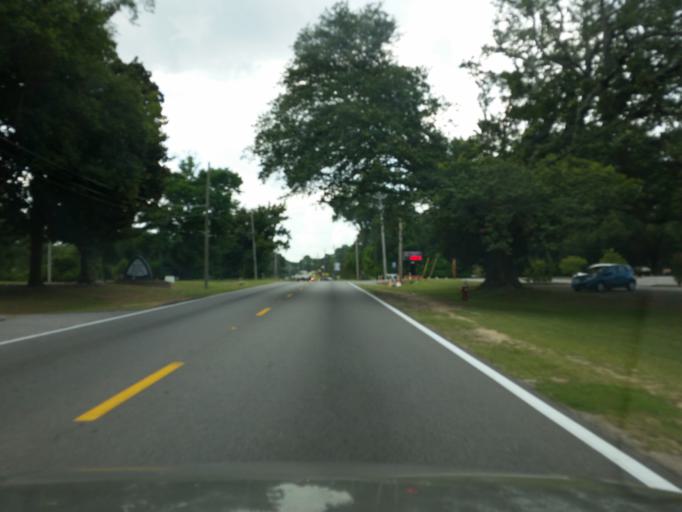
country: US
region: Florida
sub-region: Escambia County
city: Brent
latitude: 30.4867
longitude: -87.2498
